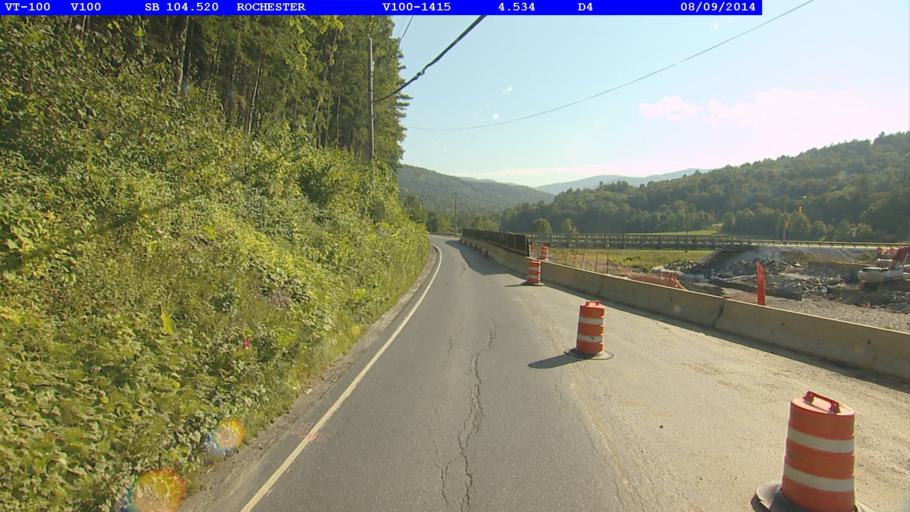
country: US
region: Vermont
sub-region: Orange County
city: Randolph
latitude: 43.8638
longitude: -72.8097
